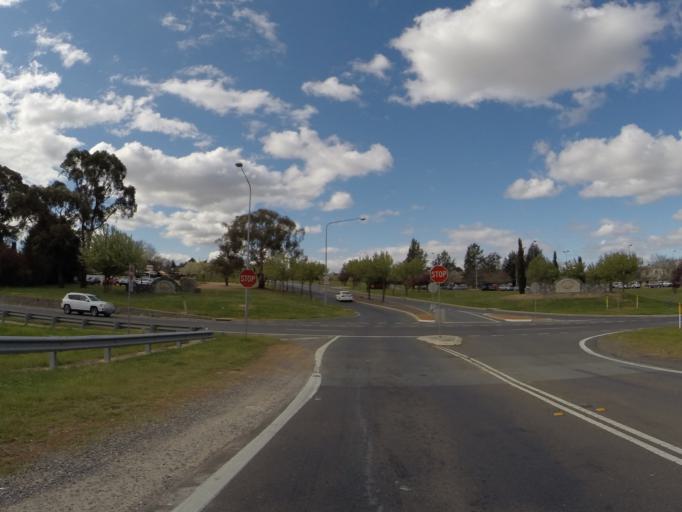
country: AU
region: Australian Capital Territory
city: Belconnen
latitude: -35.1945
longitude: 149.0861
